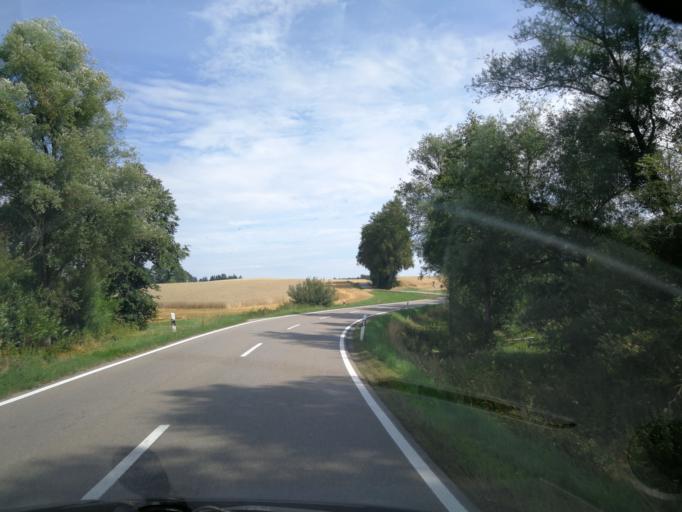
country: DE
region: Bavaria
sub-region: Lower Bavaria
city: Wiesenfelden
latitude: 49.0443
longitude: 12.5448
